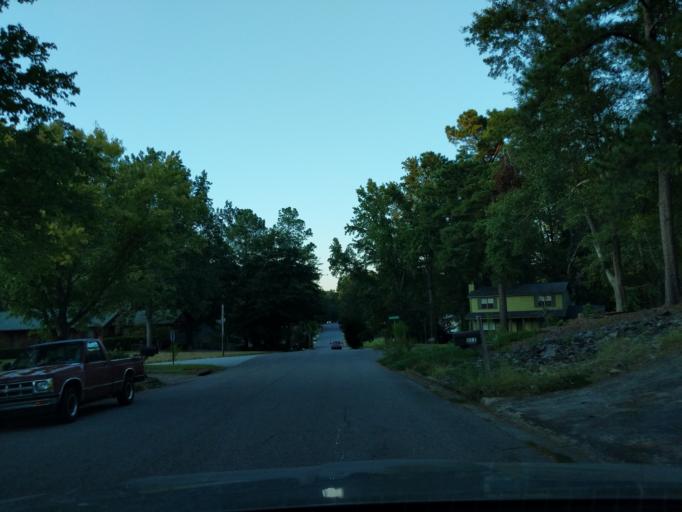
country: US
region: Georgia
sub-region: Columbia County
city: Martinez
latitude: 33.5251
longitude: -82.0903
